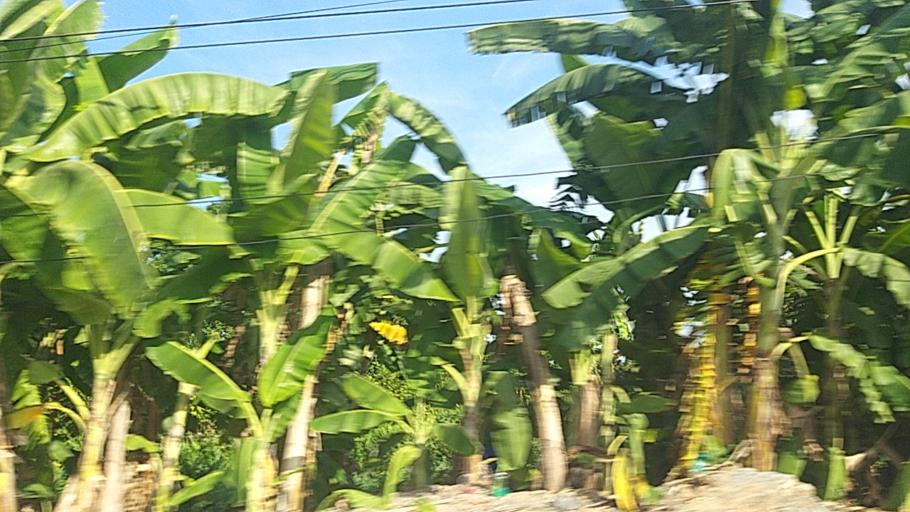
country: TH
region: Pathum Thani
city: Thanyaburi
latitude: 13.9812
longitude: 100.7292
